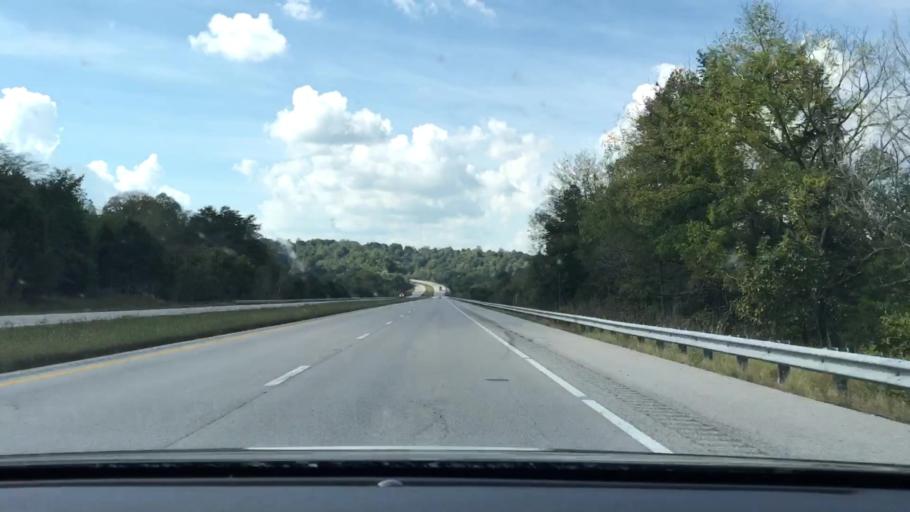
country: US
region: Kentucky
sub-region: Metcalfe County
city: Edmonton
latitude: 37.0278
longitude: -85.5372
